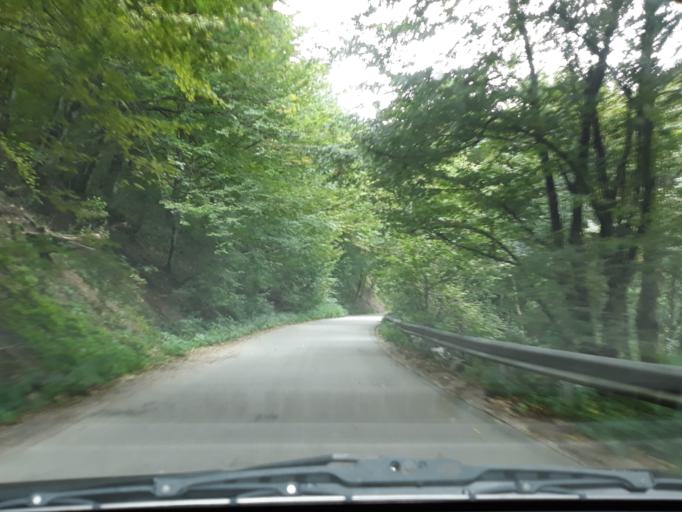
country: RO
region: Bihor
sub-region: Comuna Pietroasa
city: Pietroasa
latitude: 46.5972
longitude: 22.6374
